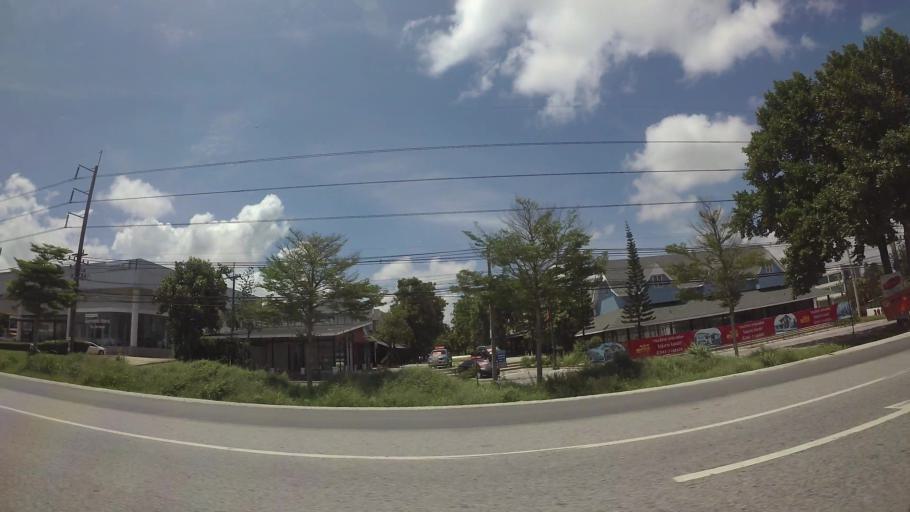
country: TH
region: Rayong
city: Rayong
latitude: 12.7163
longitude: 101.2278
